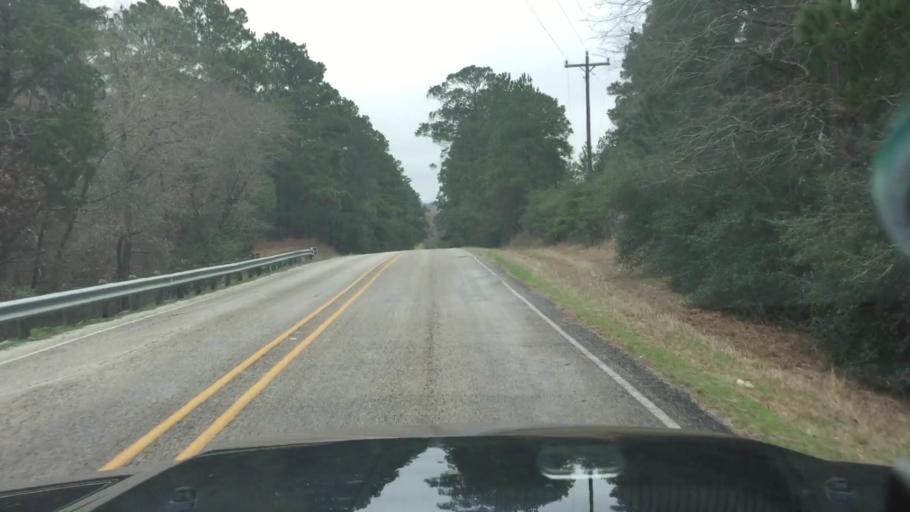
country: US
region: Texas
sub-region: Fayette County
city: La Grange
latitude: 30.0125
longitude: -96.9235
